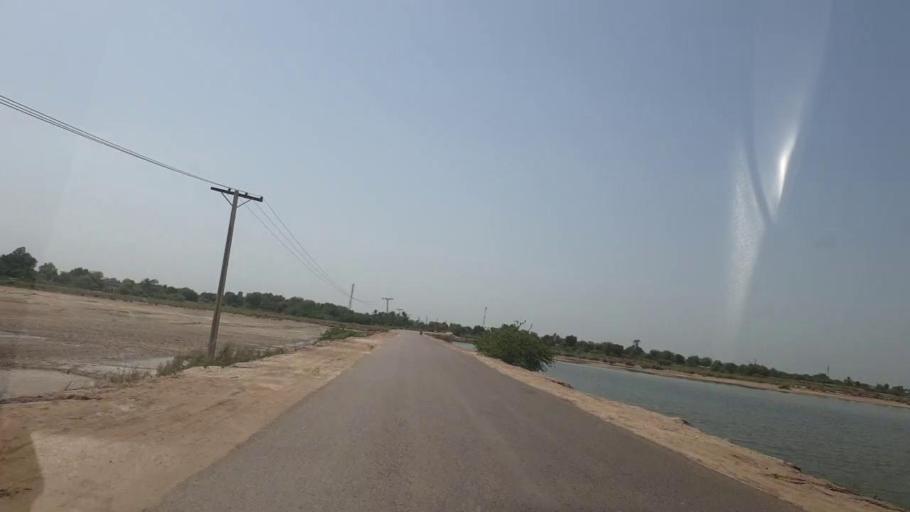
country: PK
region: Sindh
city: Bozdar
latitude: 27.1241
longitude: 68.5413
